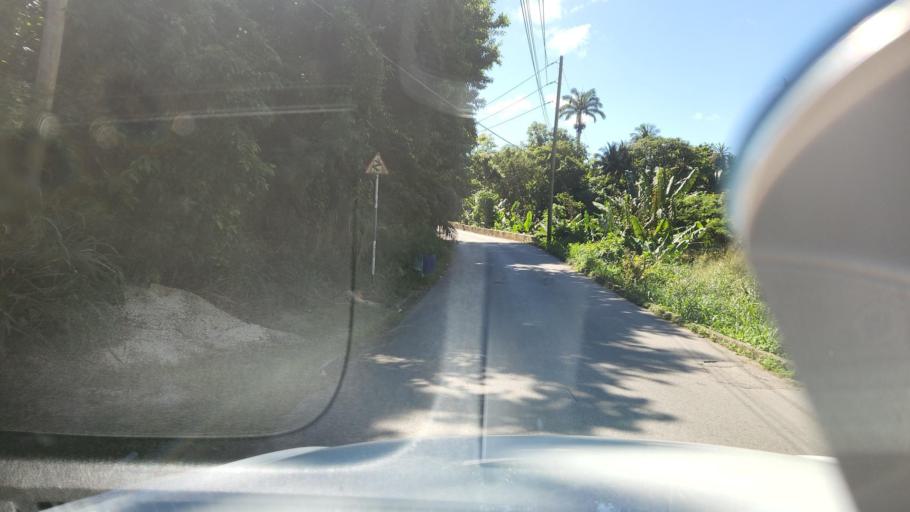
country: BB
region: Saint Thomas
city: Welchman Hall
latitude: 13.2110
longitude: -59.5916
